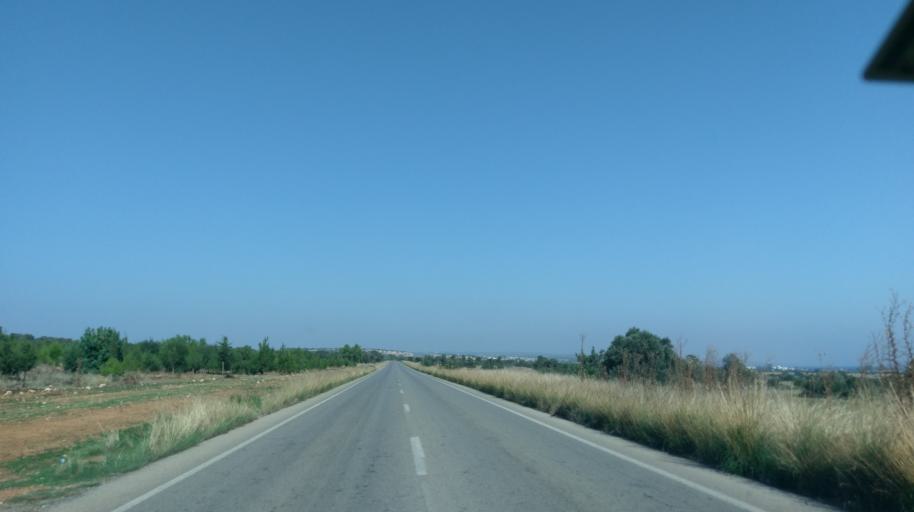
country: CY
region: Ammochostos
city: Leonarisso
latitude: 35.4045
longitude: 34.1073
